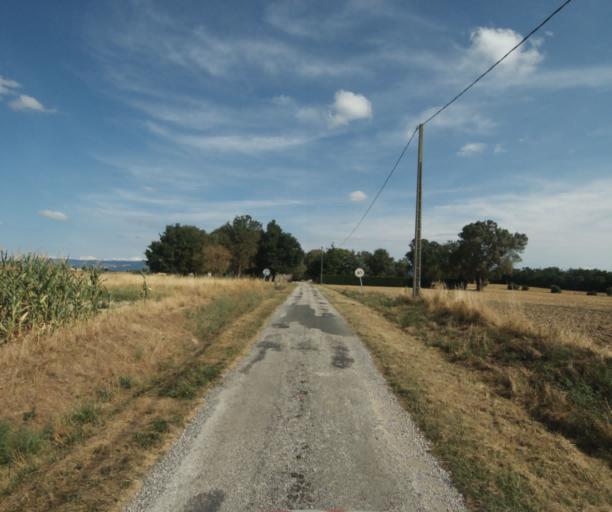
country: FR
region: Midi-Pyrenees
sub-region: Departement de la Haute-Garonne
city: Revel
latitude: 43.5122
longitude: 1.9785
